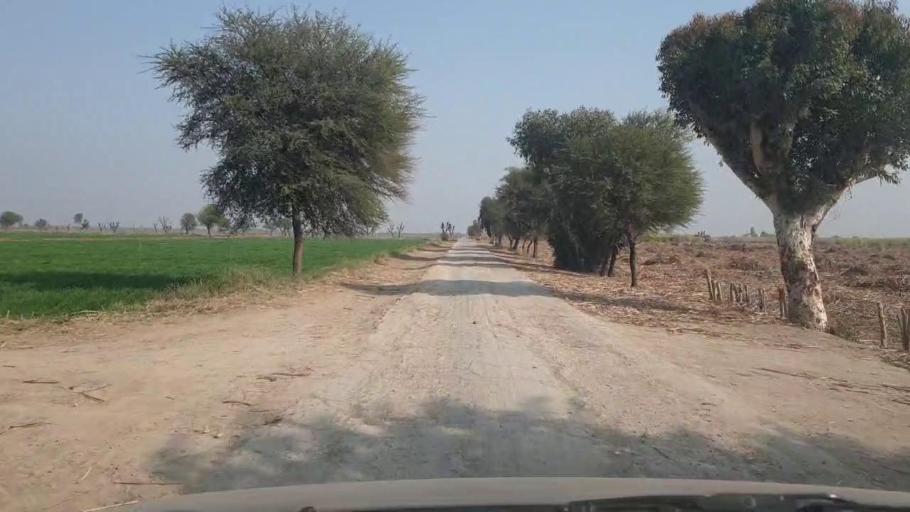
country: PK
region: Sindh
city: Mirwah Gorchani
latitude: 25.2677
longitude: 69.1616
